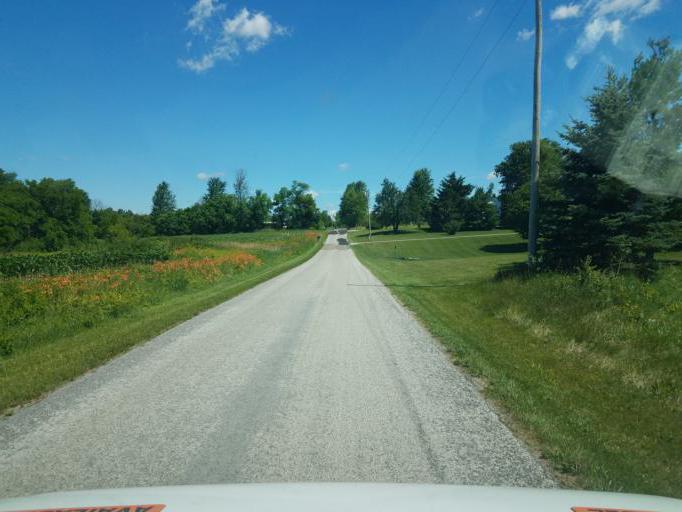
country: US
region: Ohio
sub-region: Morrow County
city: Cardington
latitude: 40.5226
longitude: -82.9341
